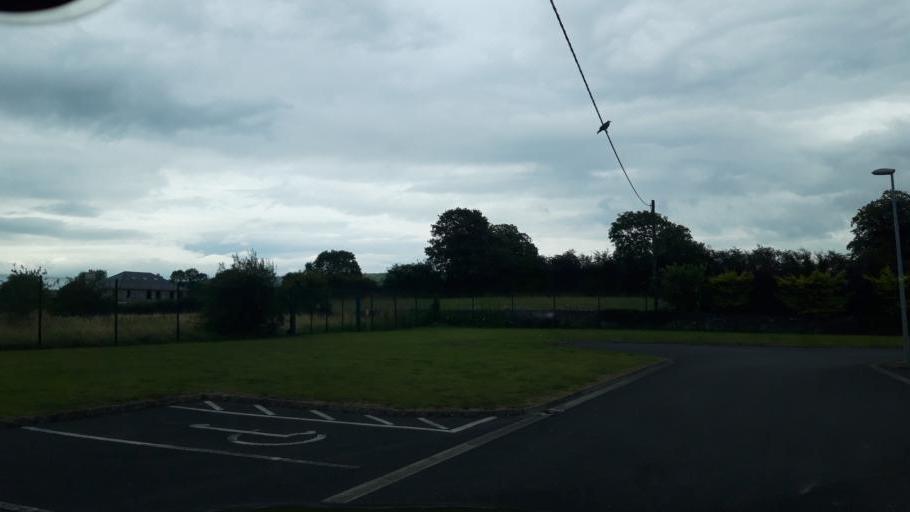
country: IE
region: Leinster
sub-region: Kilkenny
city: Ballyragget
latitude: 52.7919
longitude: -7.3306
